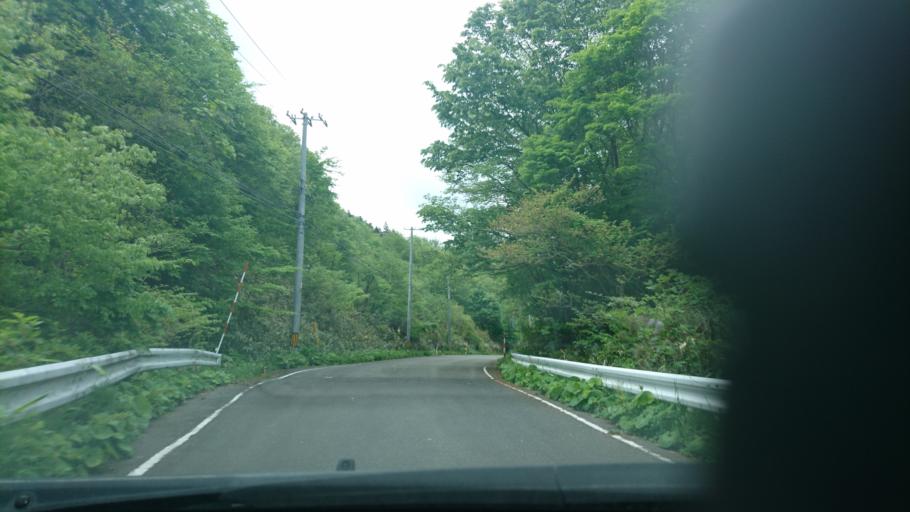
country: JP
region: Iwate
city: Ichinoseki
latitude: 38.9006
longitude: 140.9106
